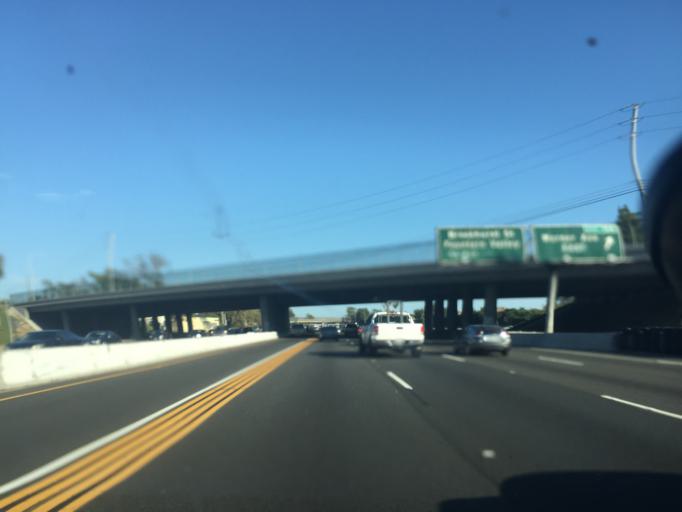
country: US
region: California
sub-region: Orange County
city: Fountain Valley
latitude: 33.7166
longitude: -117.9681
